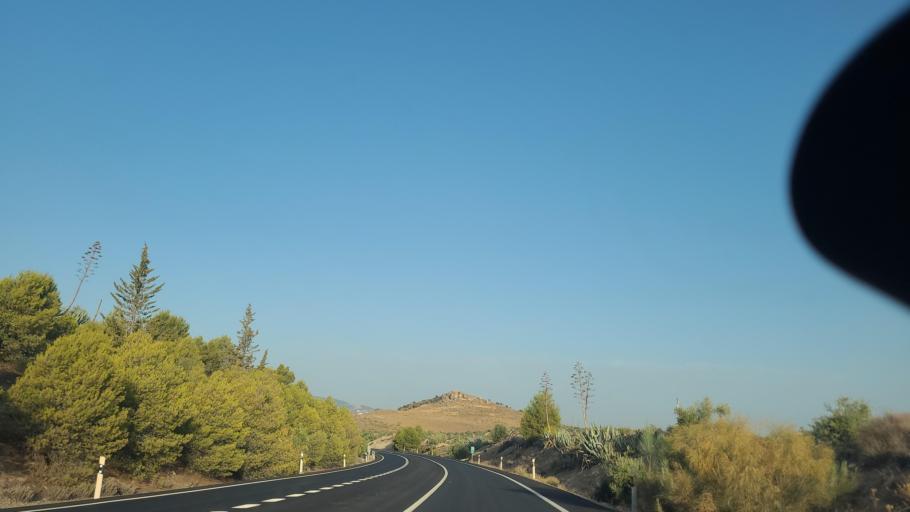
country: ES
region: Andalusia
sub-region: Provincia de Jaen
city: Mancha Real
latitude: 37.8048
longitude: -3.6523
